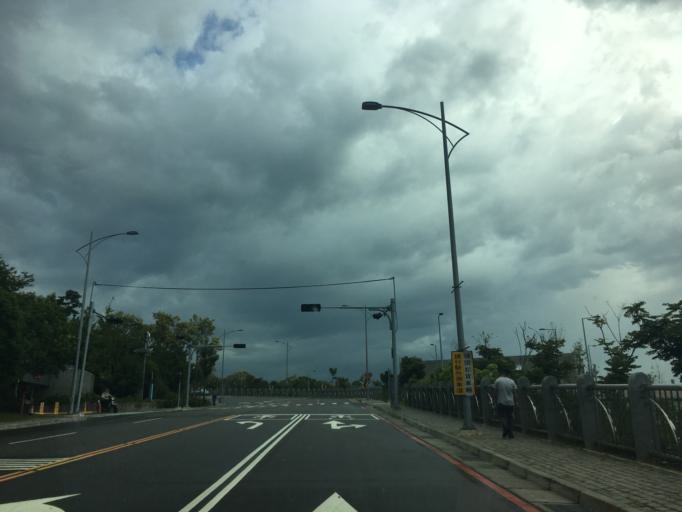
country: TW
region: Taiwan
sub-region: Taichung City
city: Taichung
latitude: 24.2108
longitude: 120.6092
